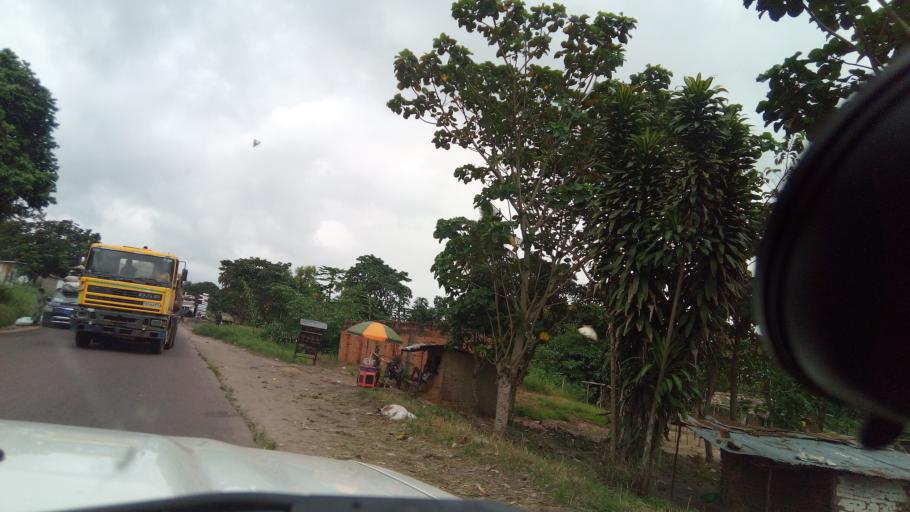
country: CD
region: Bas-Congo
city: Kasangulu
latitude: -4.8297
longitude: 15.1820
